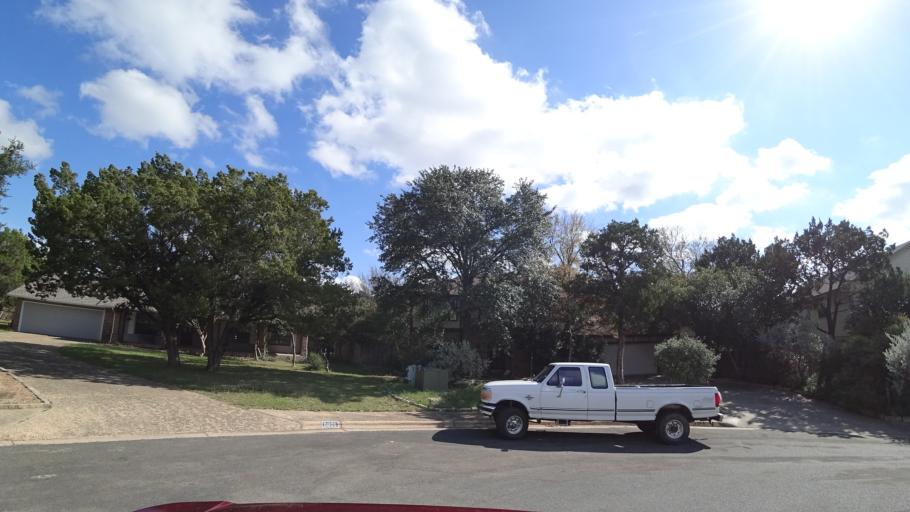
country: US
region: Texas
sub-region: Williamson County
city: Anderson Mill
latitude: 30.4221
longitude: -97.8050
